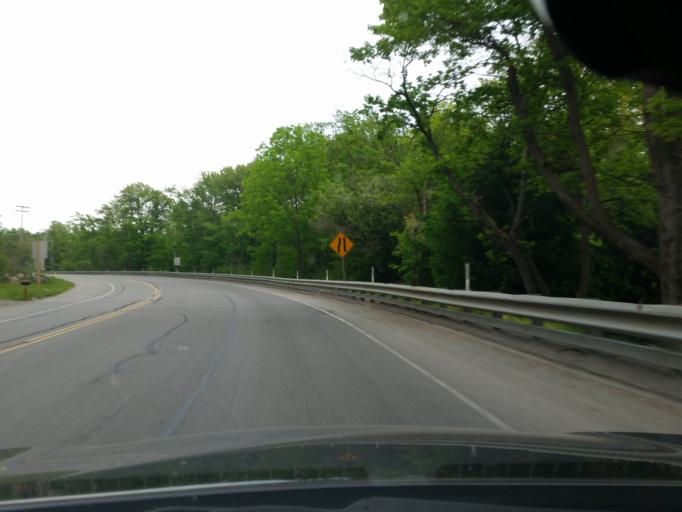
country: US
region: Pennsylvania
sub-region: Elk County
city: Ridgway
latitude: 41.4134
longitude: -78.7149
